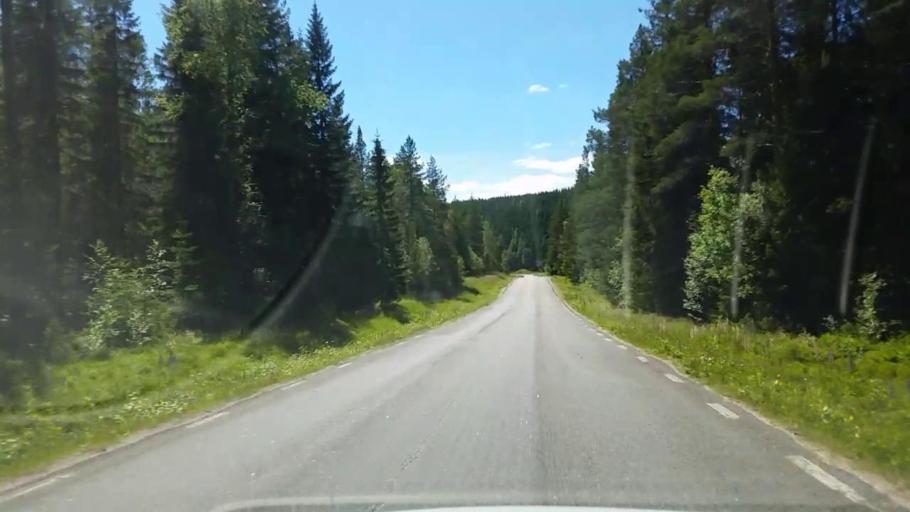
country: SE
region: Gaevleborg
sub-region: Ljusdals Kommun
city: Farila
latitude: 61.6662
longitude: 15.6088
